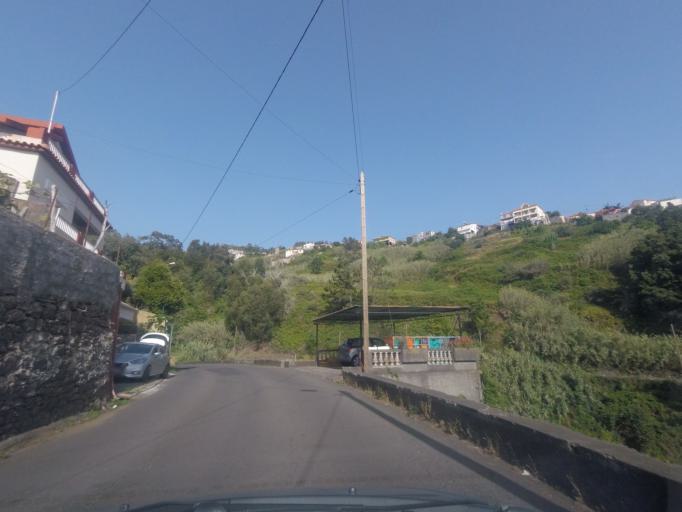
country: PT
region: Madeira
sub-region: Calheta
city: Arco da Calheta
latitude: 32.7286
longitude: -17.1530
